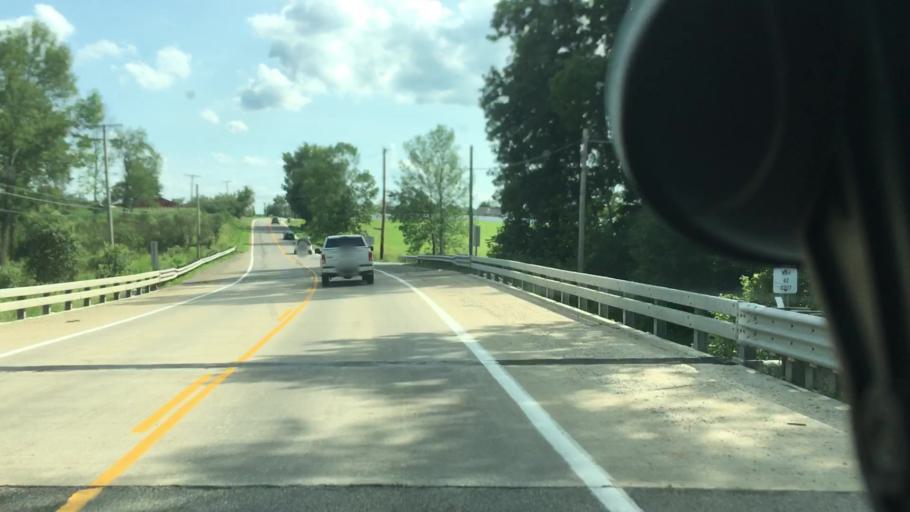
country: US
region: Ohio
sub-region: Columbiana County
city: Salem
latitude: 40.9592
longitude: -80.8314
